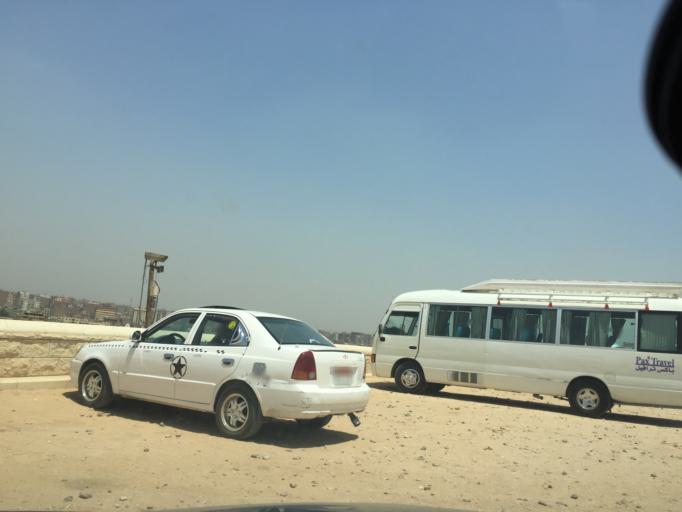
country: EG
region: Al Jizah
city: Al Jizah
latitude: 29.9815
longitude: 31.1343
